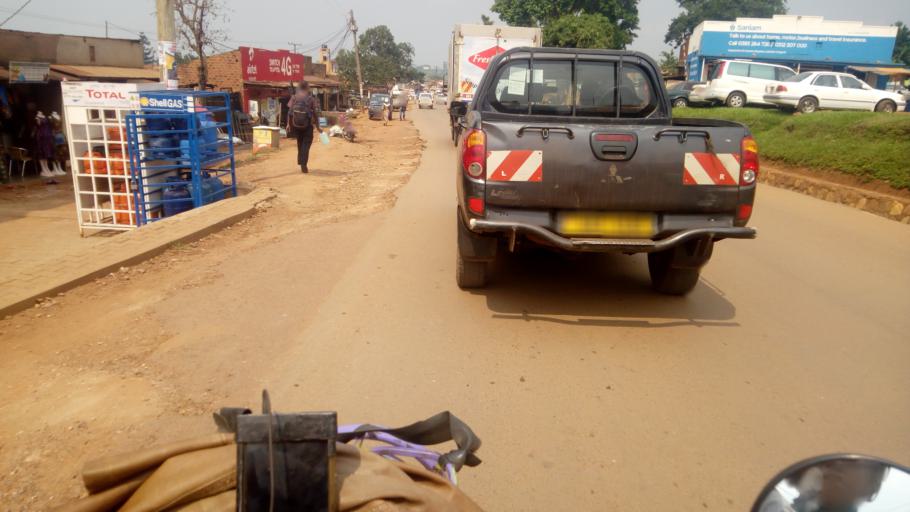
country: UG
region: Central Region
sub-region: Wakiso District
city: Kireka
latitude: 0.3204
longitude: 32.6455
